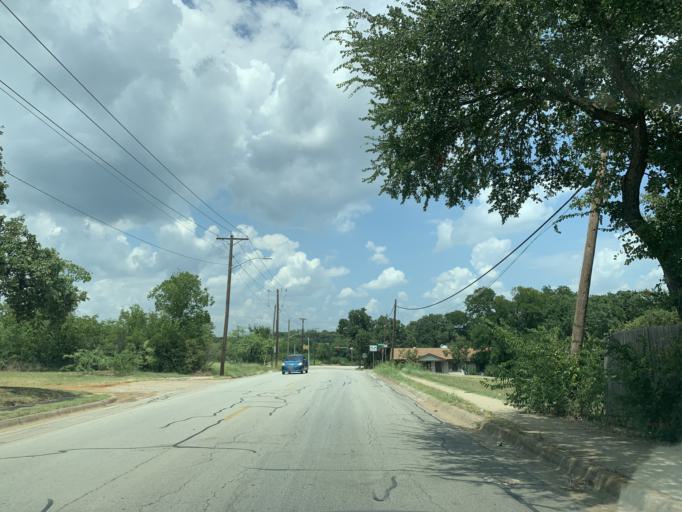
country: US
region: Texas
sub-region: Tarrant County
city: Forest Hill
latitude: 32.7288
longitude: -97.2373
